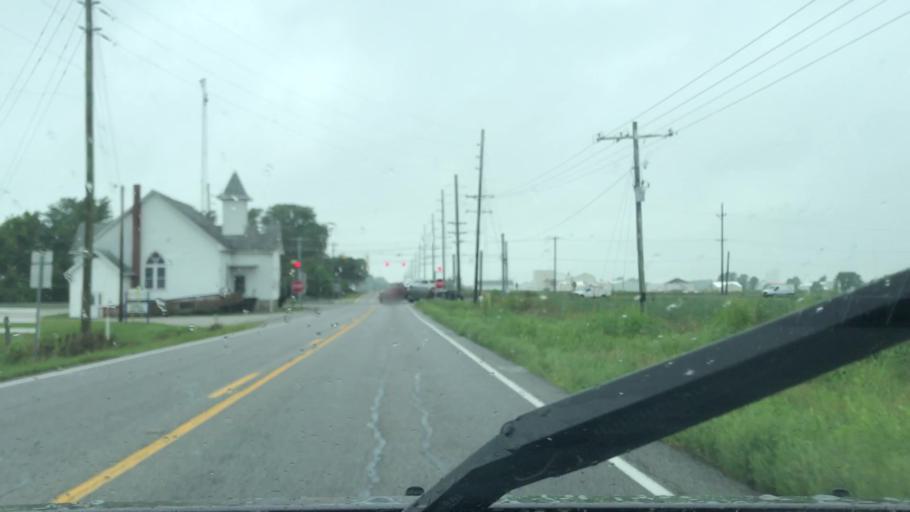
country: US
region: Indiana
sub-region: Hamilton County
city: Sheridan
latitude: 40.1281
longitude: -86.3269
